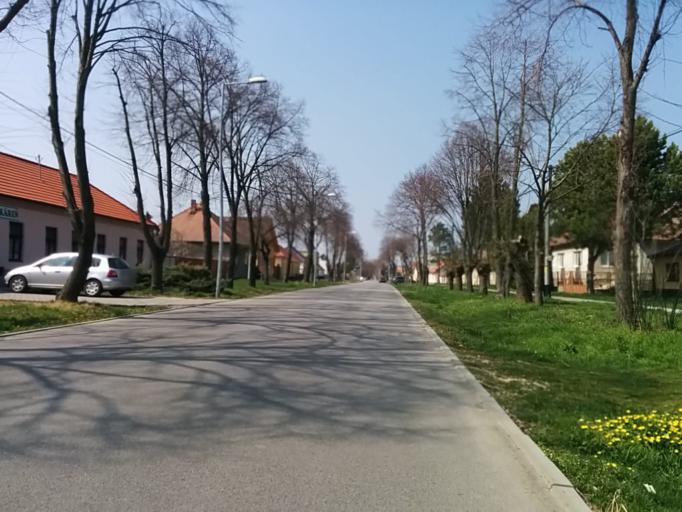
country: SK
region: Trnavsky
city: Sladkovicovo
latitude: 48.2493
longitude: 17.6194
